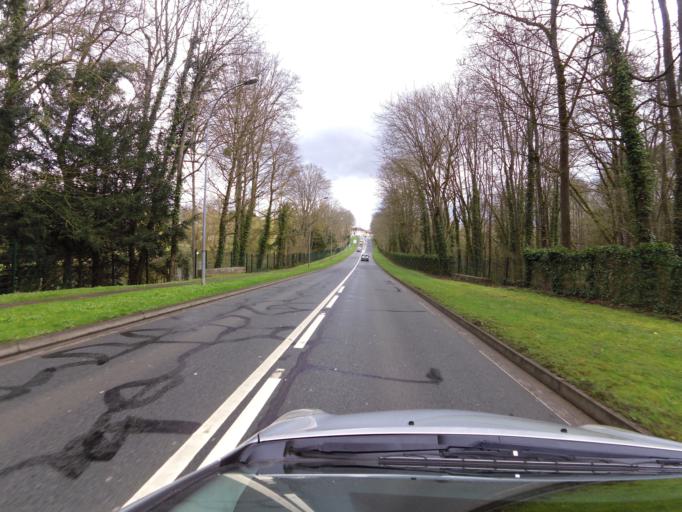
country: FR
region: Picardie
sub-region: Departement de l'Oise
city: Senlis
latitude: 49.2126
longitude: 2.5940
